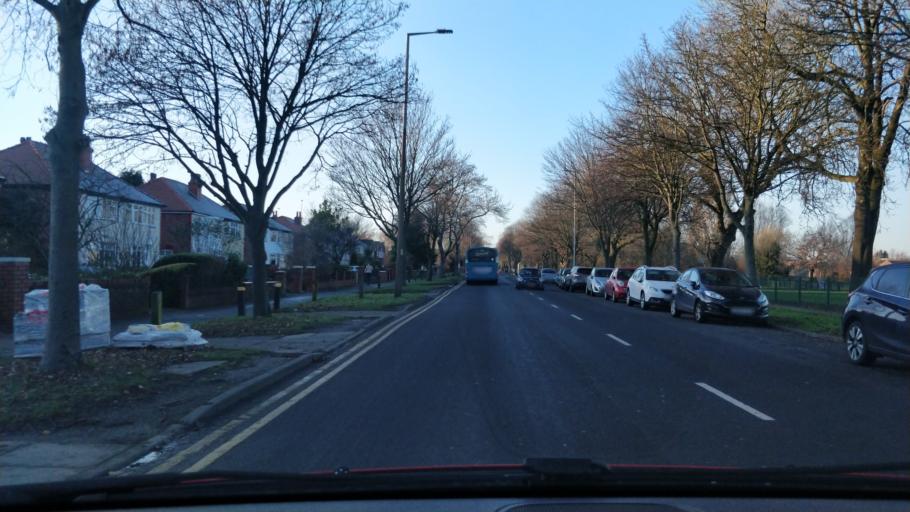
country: GB
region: England
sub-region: Sefton
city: Southport
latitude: 53.6346
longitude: -2.9747
